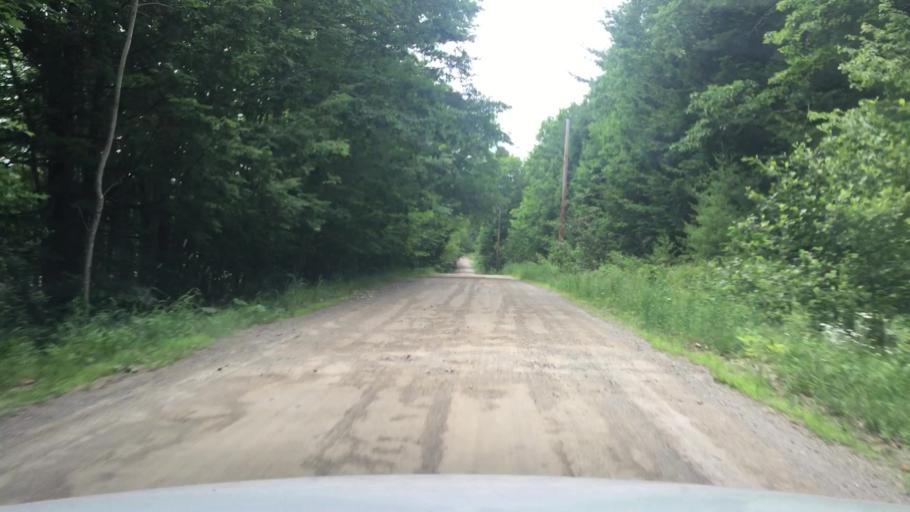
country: US
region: Maine
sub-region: Waldo County
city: Searsmont
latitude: 44.4249
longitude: -69.2572
